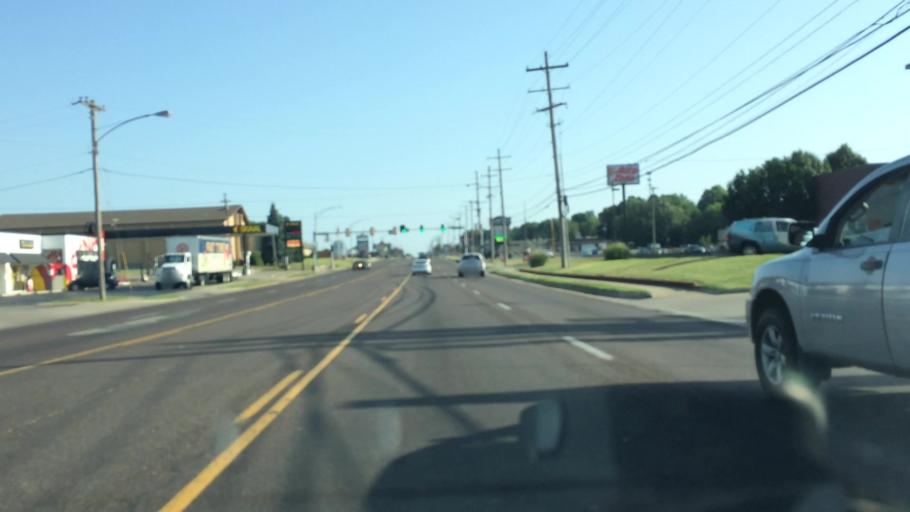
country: US
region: Missouri
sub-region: Greene County
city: Springfield
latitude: 37.1700
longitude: -93.2954
